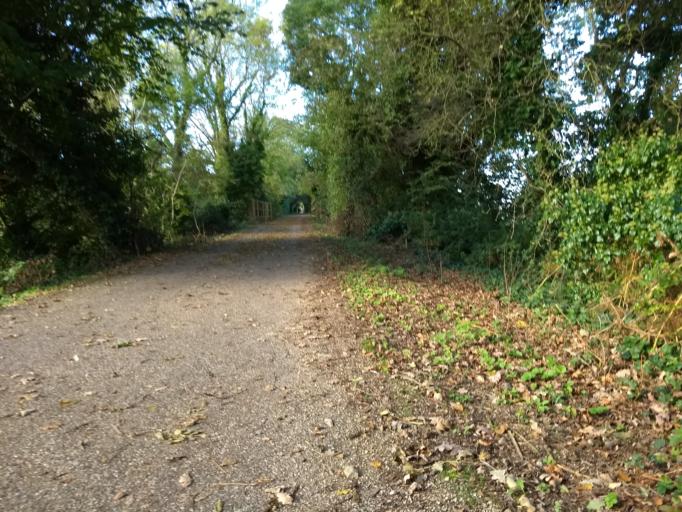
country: GB
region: England
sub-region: Isle of Wight
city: Shanklin
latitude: 50.6295
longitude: -1.2021
